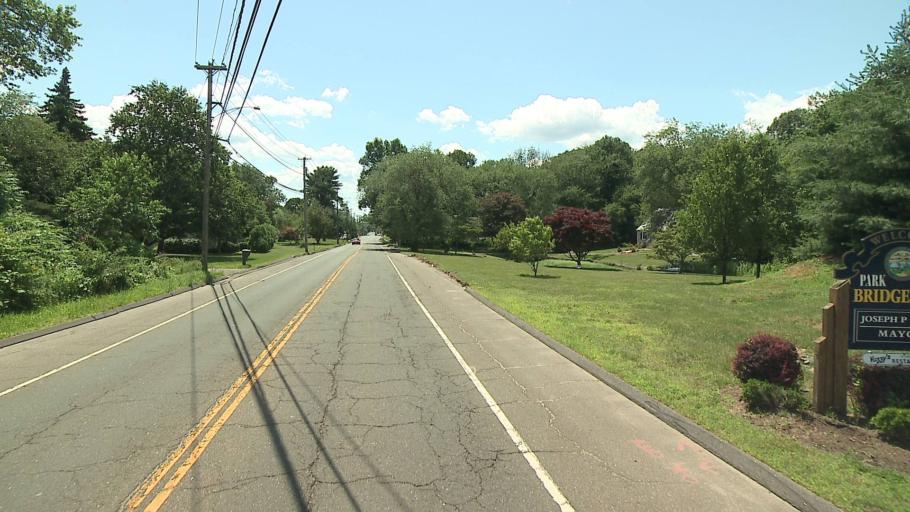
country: US
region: Connecticut
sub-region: Fairfield County
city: Trumbull
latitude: 41.2243
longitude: -73.1671
